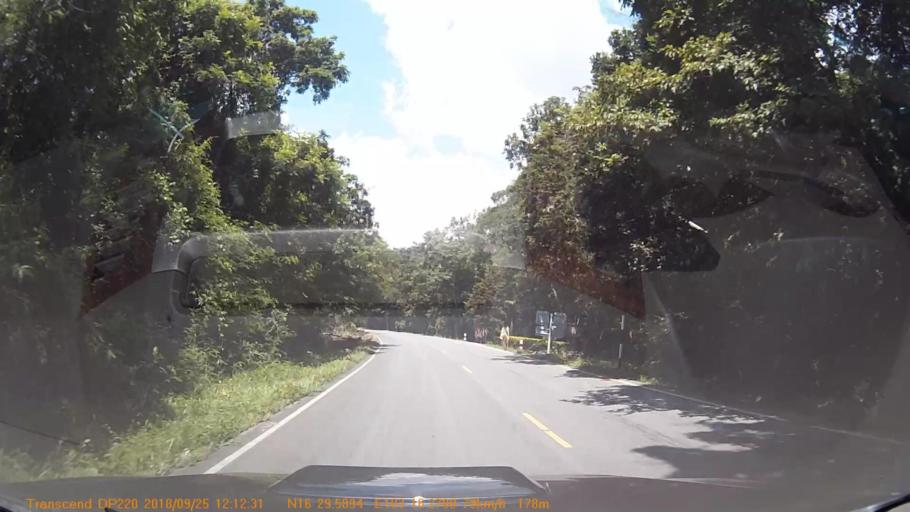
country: TH
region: Kalasin
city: Huai Mek
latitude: 16.4933
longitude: 103.2712
